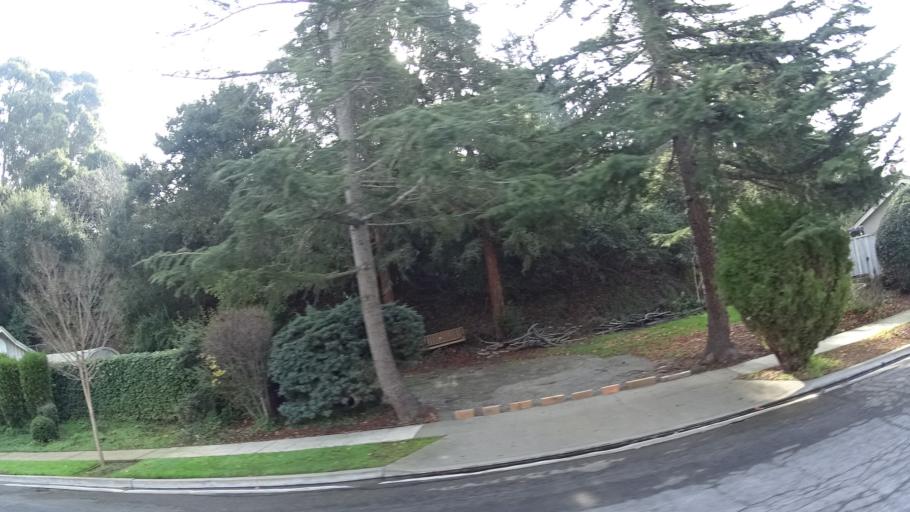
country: US
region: California
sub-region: Alameda County
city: Hayward
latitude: 37.6635
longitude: -122.0712
